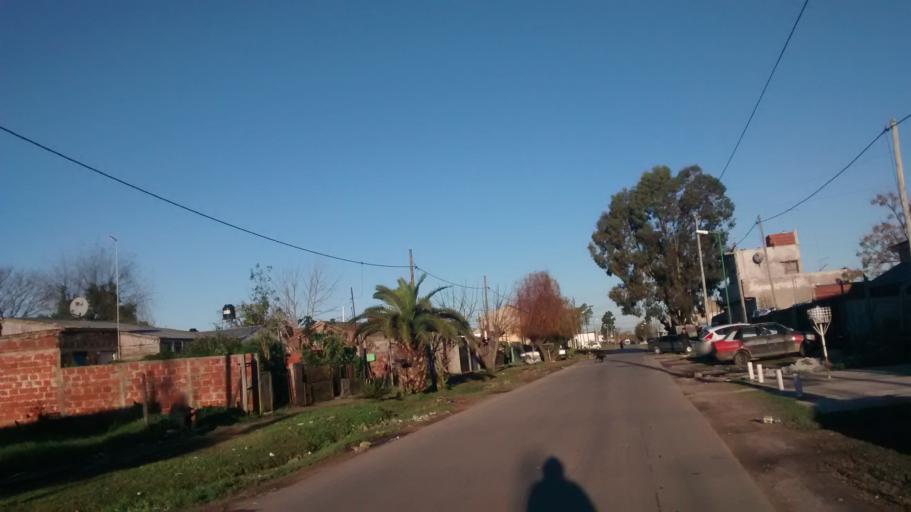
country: AR
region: Buenos Aires
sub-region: Partido de La Plata
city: La Plata
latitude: -34.9577
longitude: -57.9379
